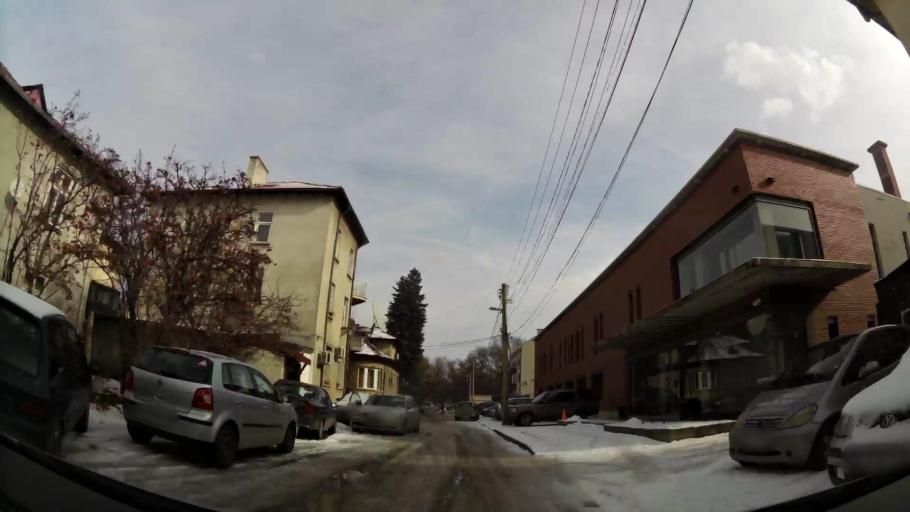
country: BG
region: Sofia-Capital
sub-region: Stolichna Obshtina
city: Sofia
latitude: 42.7021
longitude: 23.3466
